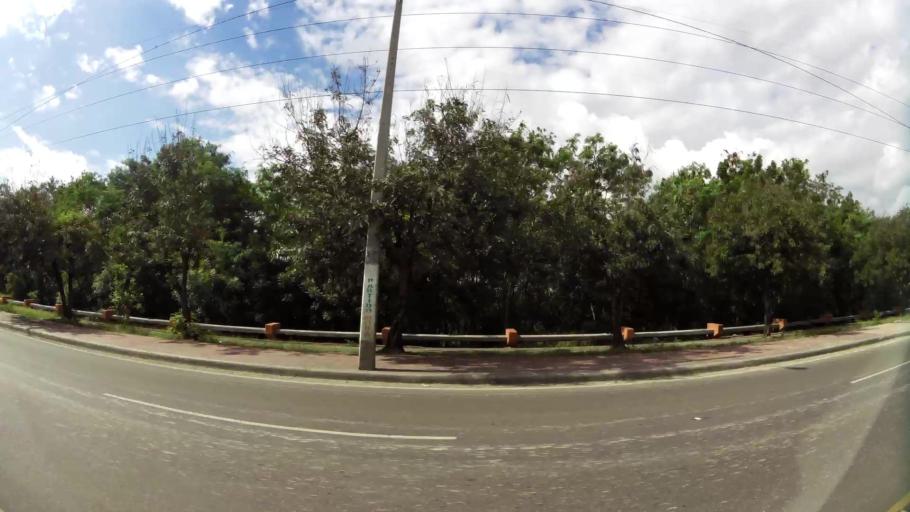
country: DO
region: Santiago
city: Santiago de los Caballeros
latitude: 19.4688
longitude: -70.7151
